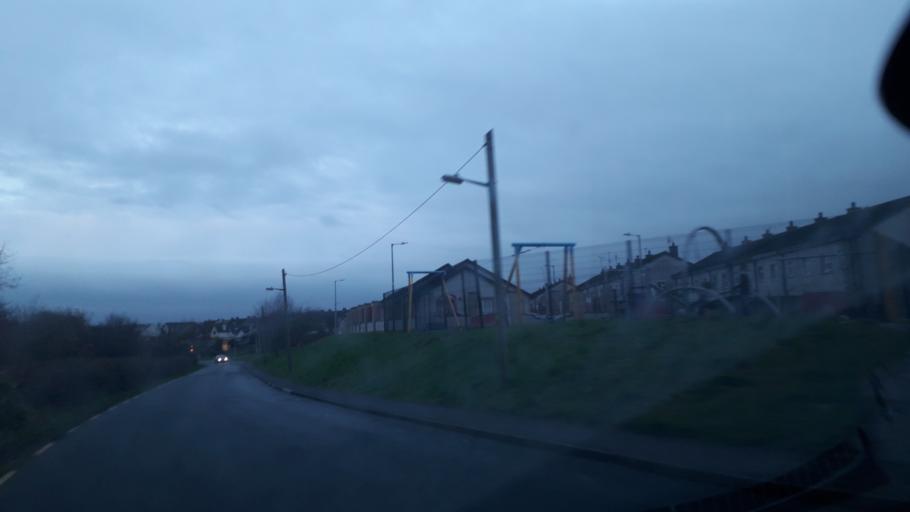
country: IE
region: Leinster
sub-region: Kilkenny
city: Kilkenny
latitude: 52.6626
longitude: -7.2463
